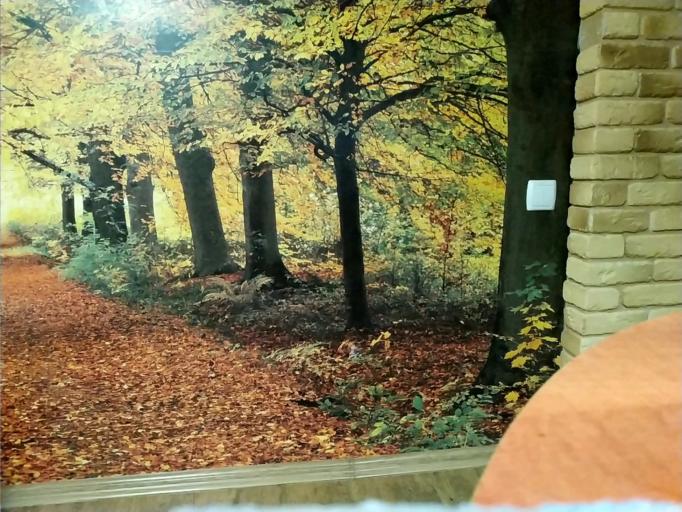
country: BY
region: Minsk
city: Plyeshchanitsy
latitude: 54.4268
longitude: 27.5904
